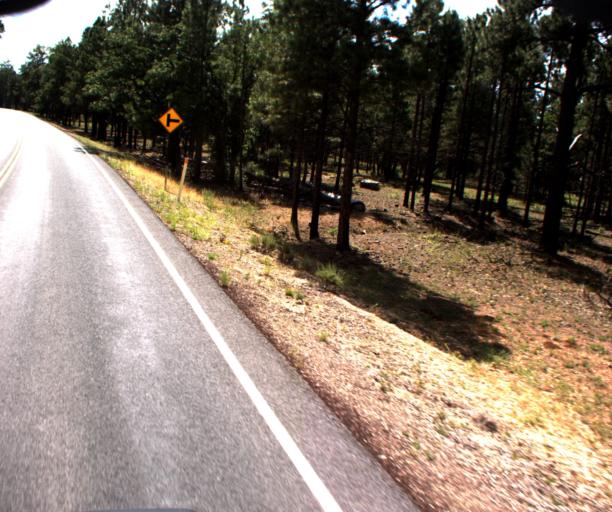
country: US
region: Arizona
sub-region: Coconino County
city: Grand Canyon
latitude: 35.9685
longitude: -111.9745
